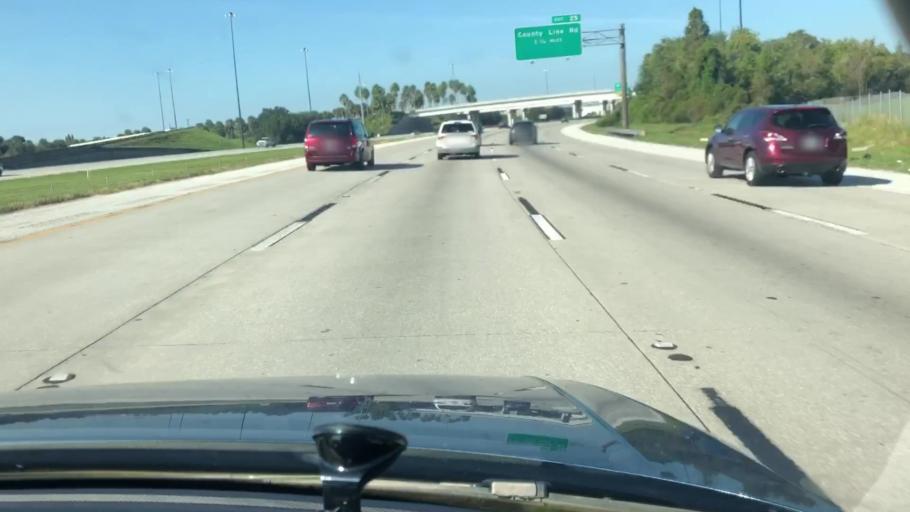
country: US
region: Florida
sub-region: Polk County
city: Winston
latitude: 28.0377
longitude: -82.0364
